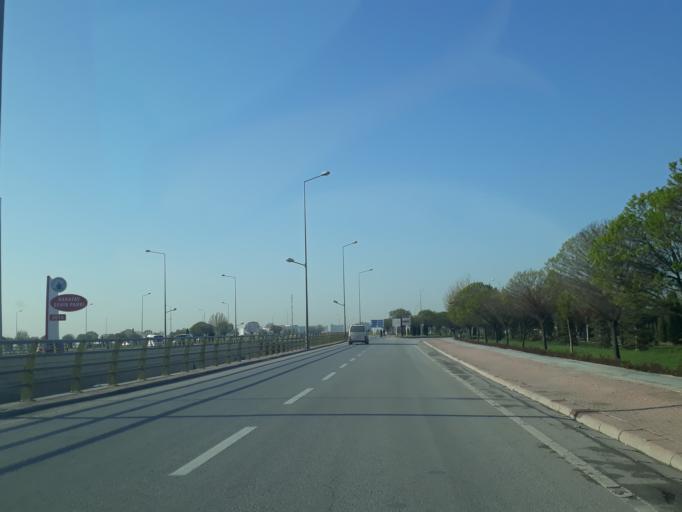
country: TR
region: Konya
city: Selcuklu
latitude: 37.8714
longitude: 32.5480
